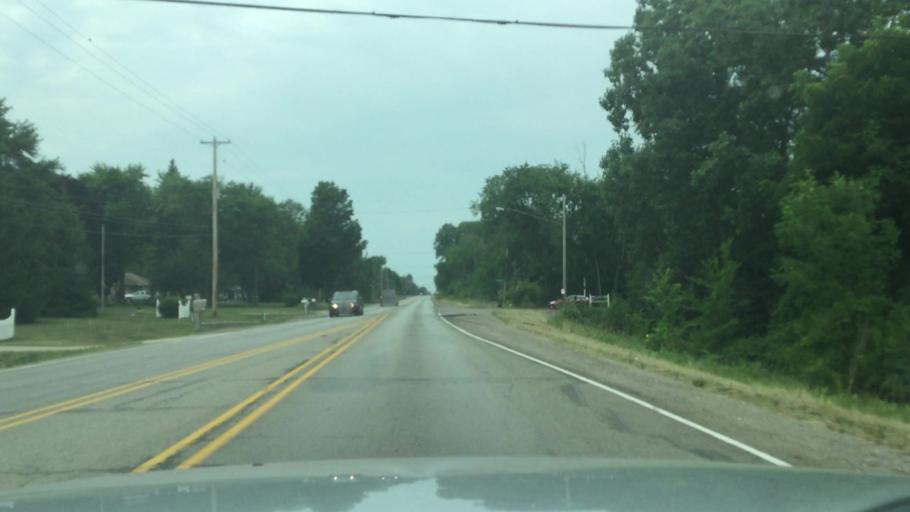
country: US
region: Michigan
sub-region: Genesee County
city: Flint
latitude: 42.9596
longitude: -83.6945
